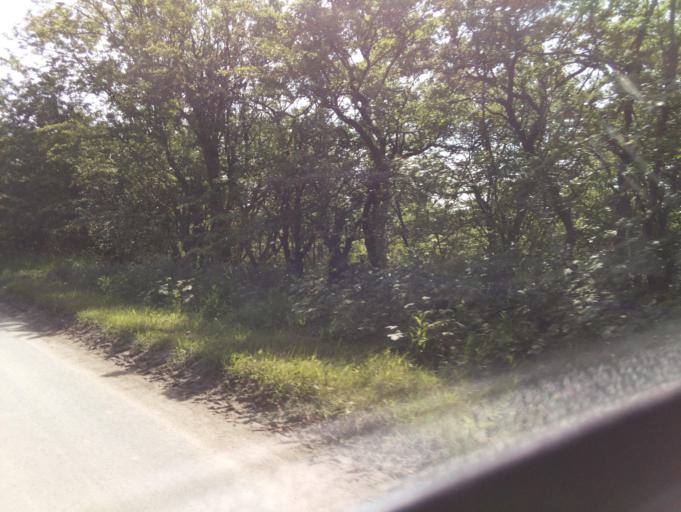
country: GB
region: England
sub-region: North Lincolnshire
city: Manton
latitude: 53.5002
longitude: -0.5802
